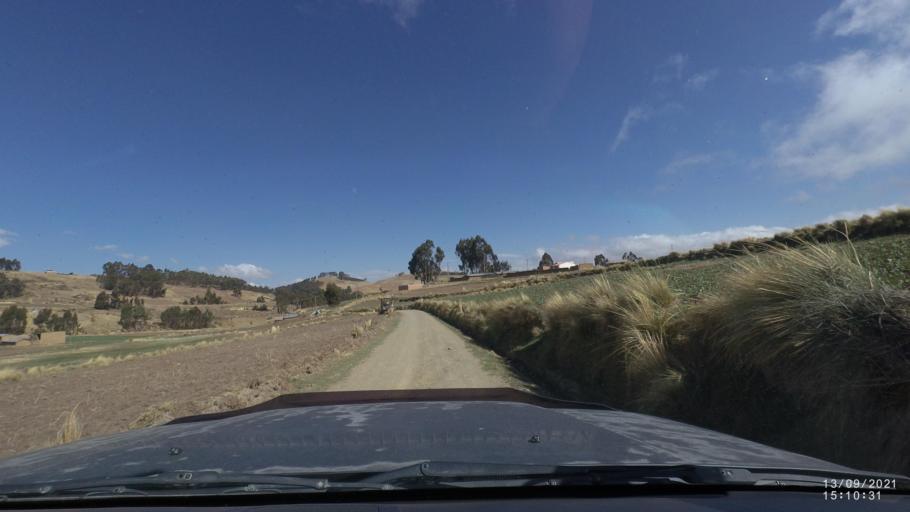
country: BO
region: Cochabamba
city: Colomi
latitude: -17.3550
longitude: -65.8049
